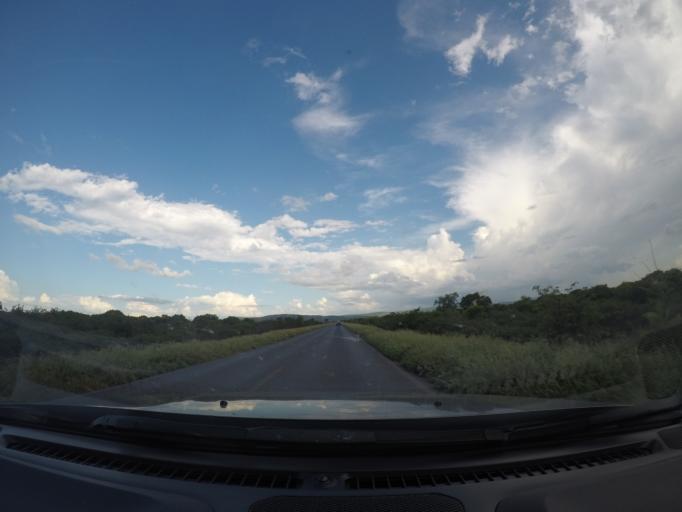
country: BR
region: Bahia
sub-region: Ibotirama
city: Ibotirama
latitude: -12.1782
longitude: -43.2450
